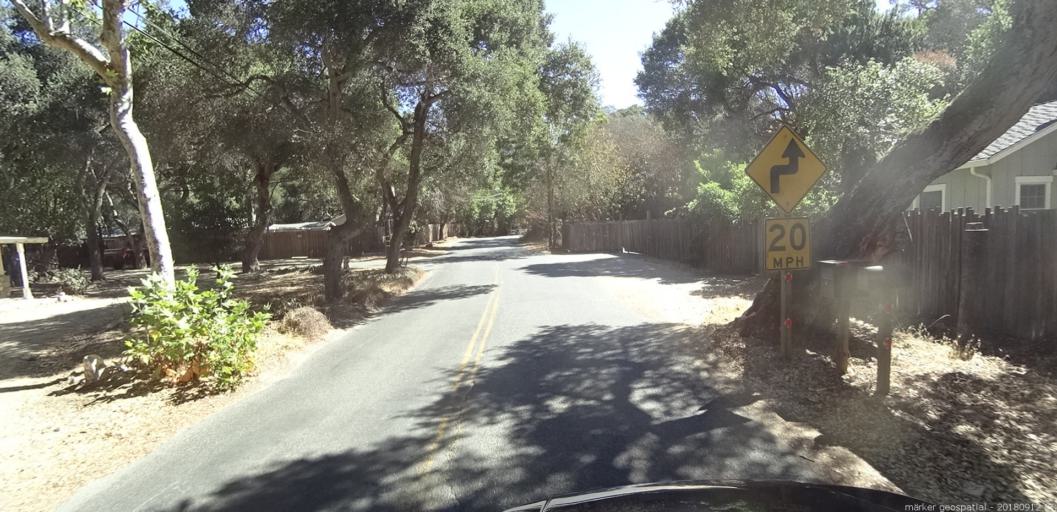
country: US
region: California
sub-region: Monterey County
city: Carmel Valley Village
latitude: 36.4733
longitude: -121.7264
